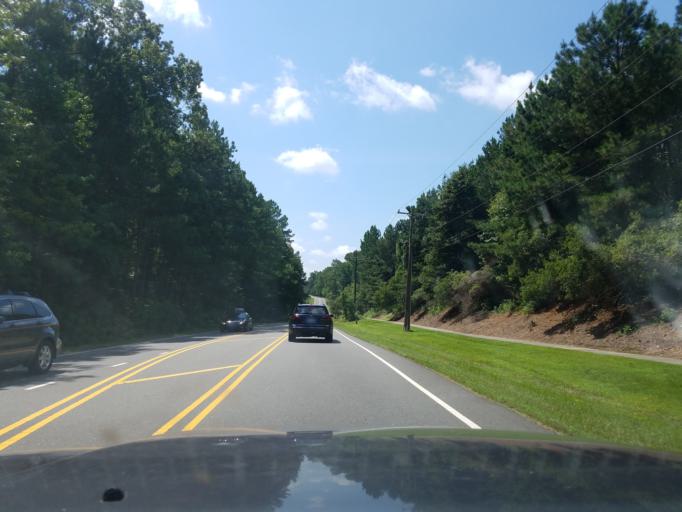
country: US
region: North Carolina
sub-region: Durham County
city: Durham
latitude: 35.9414
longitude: -78.9657
